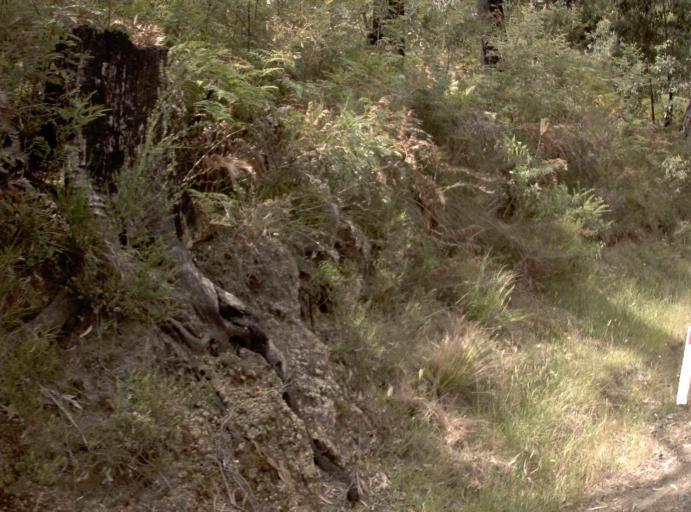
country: AU
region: Victoria
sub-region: Latrobe
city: Traralgon
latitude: -38.3155
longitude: 146.5700
